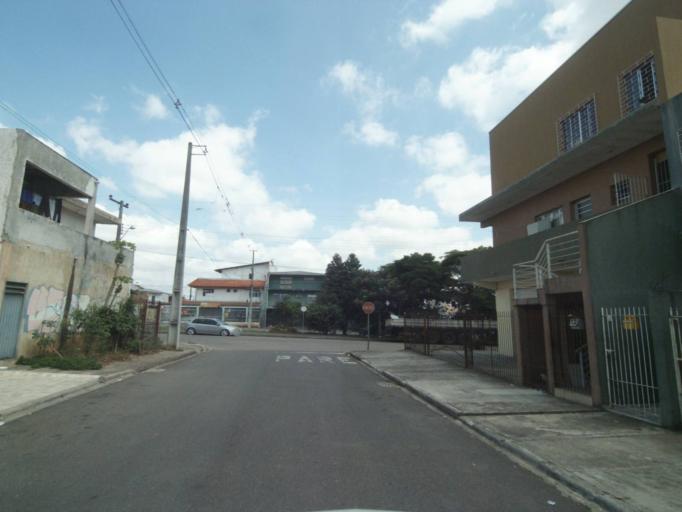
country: BR
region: Parana
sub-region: Sao Jose Dos Pinhais
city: Sao Jose dos Pinhais
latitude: -25.5408
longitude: -49.2631
